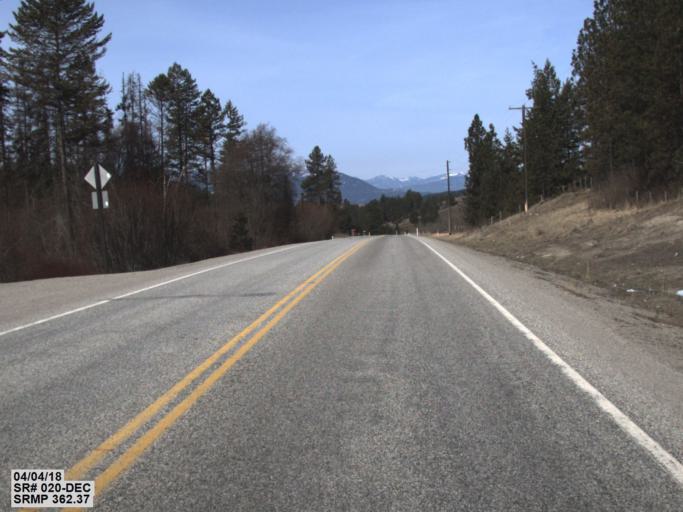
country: US
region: Washington
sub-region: Stevens County
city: Colville
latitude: 48.5153
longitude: -117.7611
